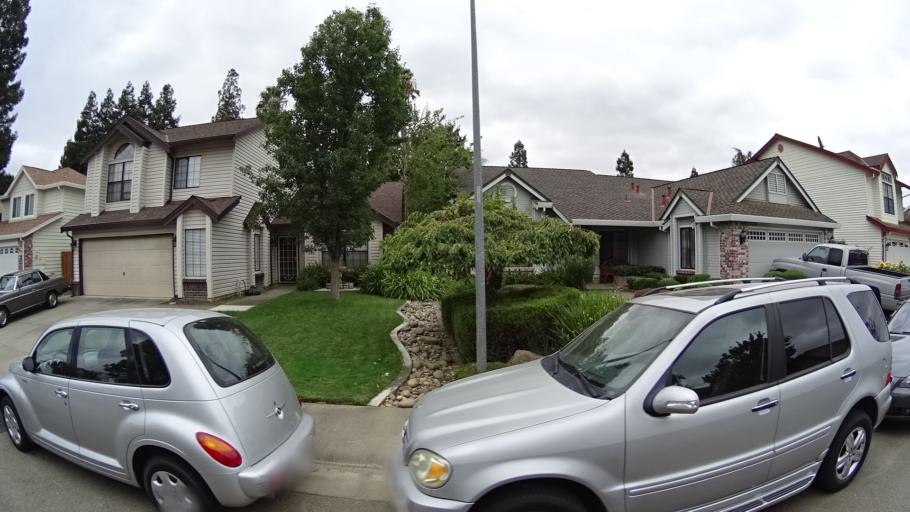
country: US
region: California
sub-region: Sacramento County
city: Laguna
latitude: 38.4214
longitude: -121.4397
